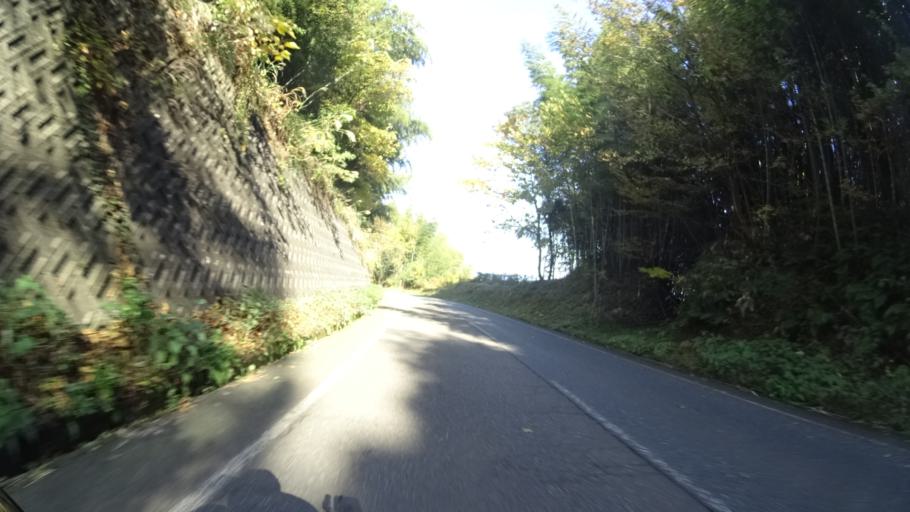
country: JP
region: Niigata
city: Itoigawa
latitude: 37.0353
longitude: 137.8836
